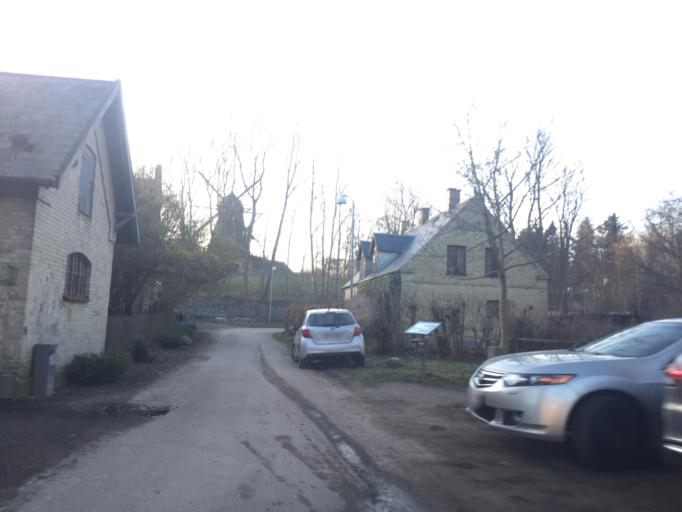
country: DK
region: Capital Region
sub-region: Lyngby-Tarbaek Kommune
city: Kongens Lyngby
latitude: 55.7848
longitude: 12.4962
